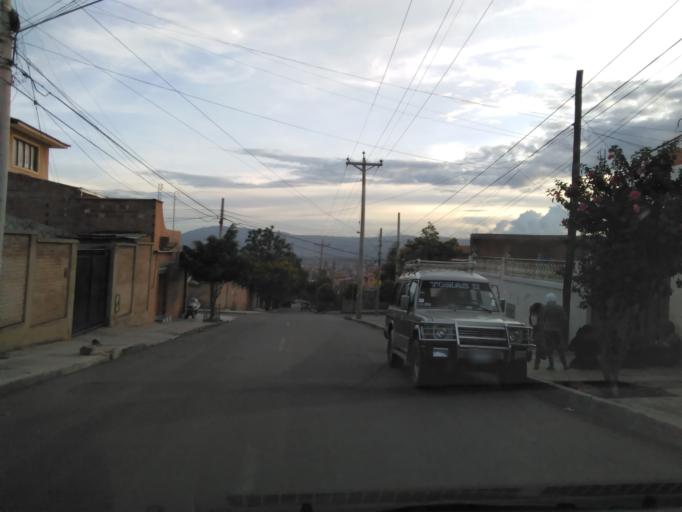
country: BO
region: Cochabamba
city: Cochabamba
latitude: -17.3583
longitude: -66.1609
